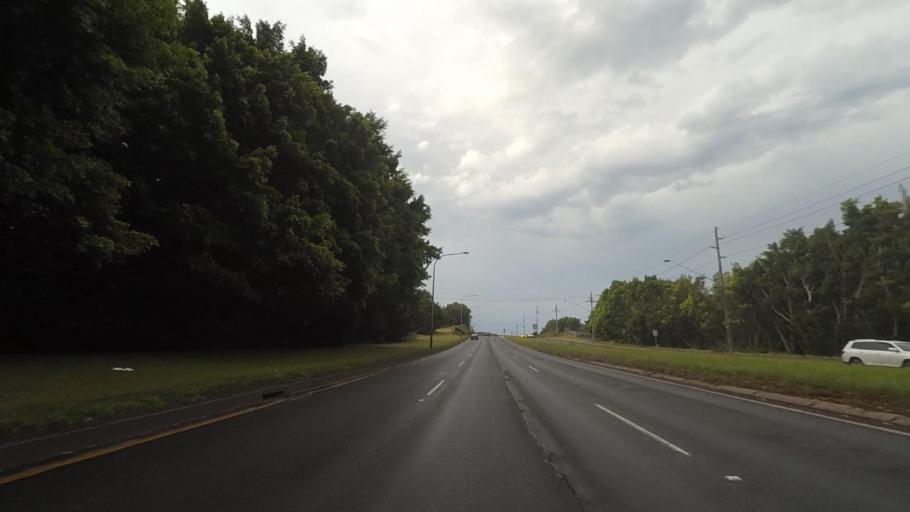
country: AU
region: New South Wales
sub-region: Wollongong
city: Coniston
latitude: -34.4530
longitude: 150.8740
